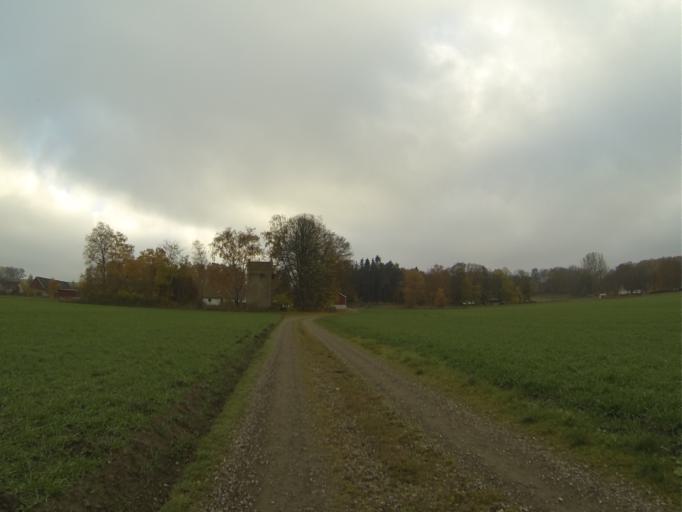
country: SE
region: Skane
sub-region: Lunds Kommun
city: Genarp
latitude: 55.7095
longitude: 13.3785
